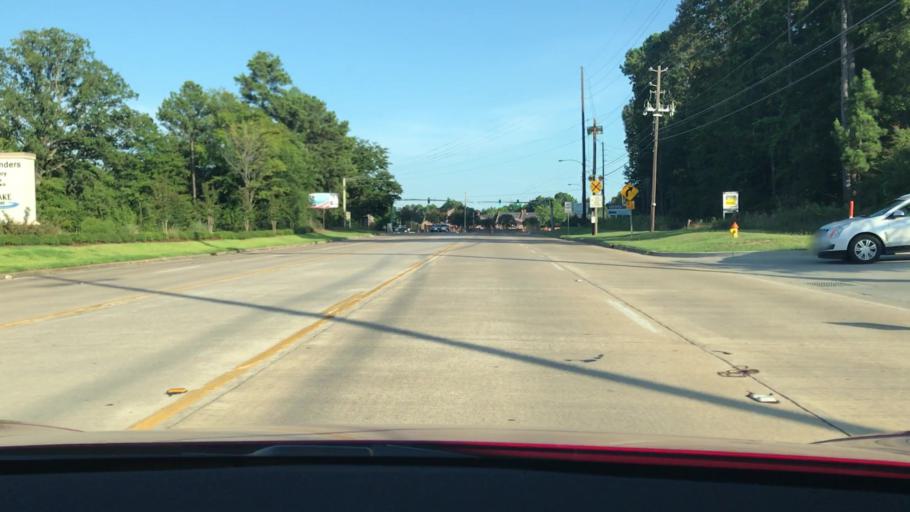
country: US
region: Louisiana
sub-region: Bossier Parish
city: Bossier City
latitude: 32.4225
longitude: -93.7375
